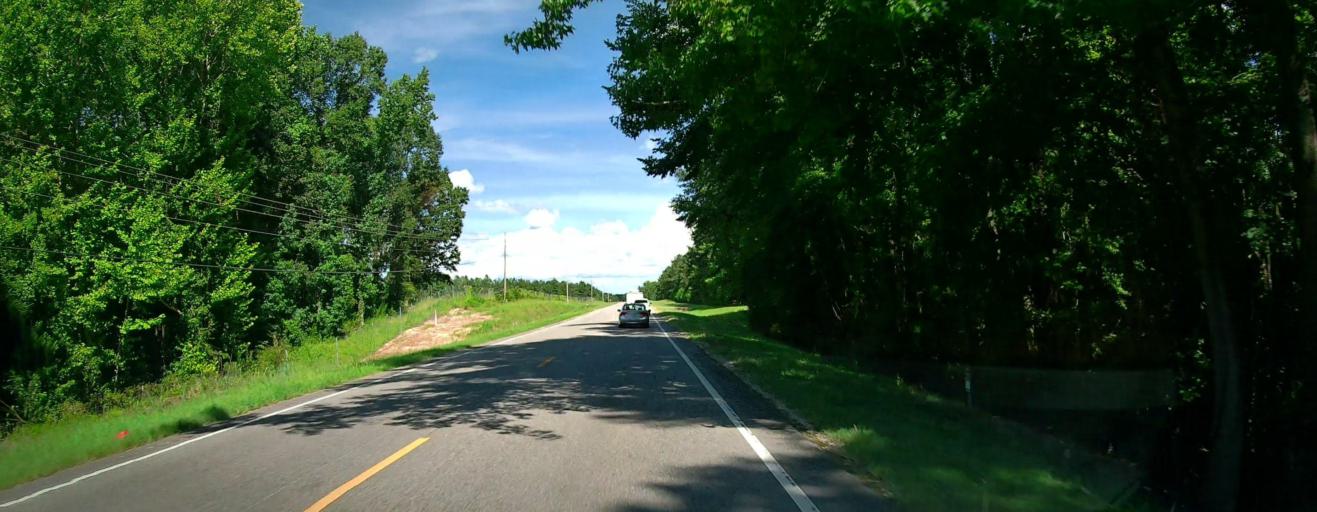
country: US
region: Alabama
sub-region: Macon County
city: Tuskegee
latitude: 32.3829
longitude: -85.8058
